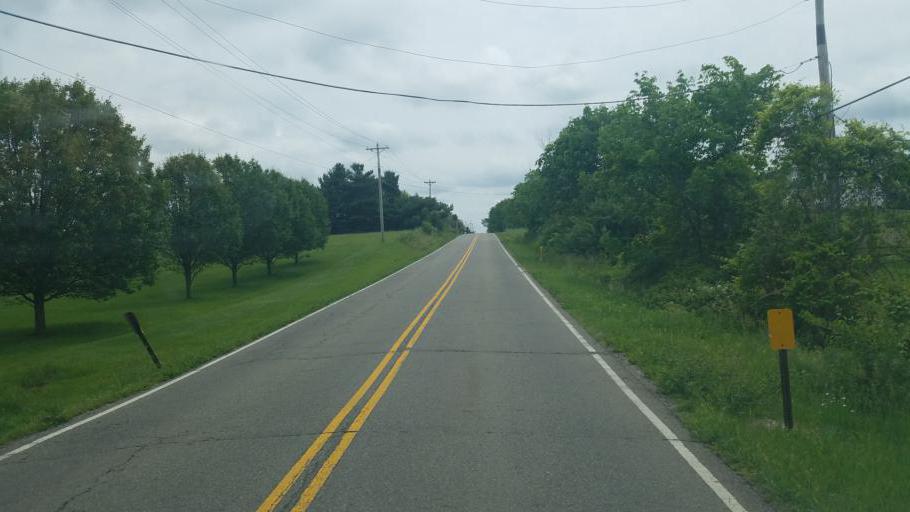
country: US
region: Ohio
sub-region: Licking County
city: Johnstown
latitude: 40.1571
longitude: -82.6223
